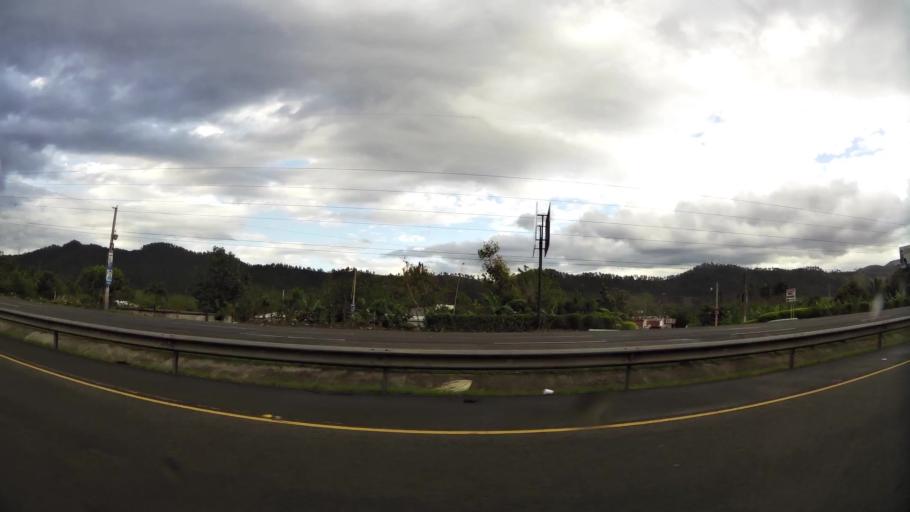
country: DO
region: Monsenor Nouel
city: Bonao
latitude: 18.9272
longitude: -70.3825
